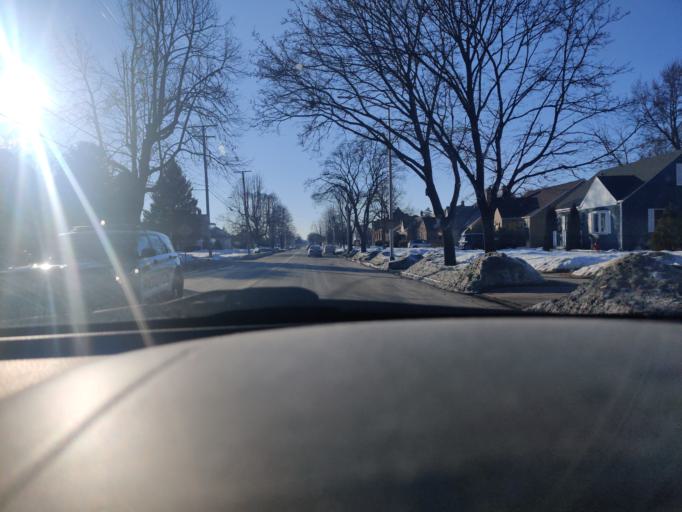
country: US
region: Wisconsin
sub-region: Kenosha County
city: Kenosha
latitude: 42.5659
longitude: -87.8311
